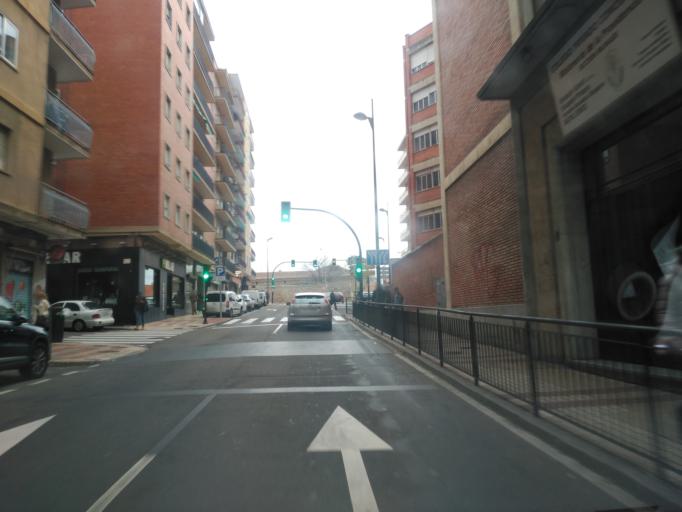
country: ES
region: Castille and Leon
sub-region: Provincia de Salamanca
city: Salamanca
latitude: 40.9665
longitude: -5.6720
